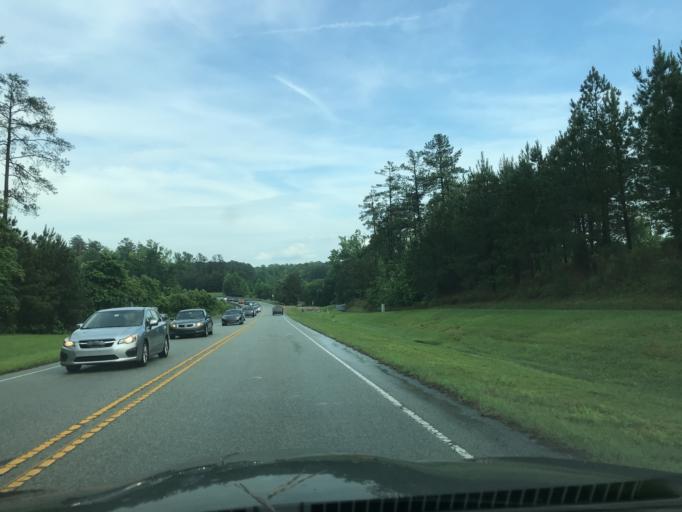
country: US
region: North Carolina
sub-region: Wake County
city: Morrisville
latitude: 35.8582
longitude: -78.8830
